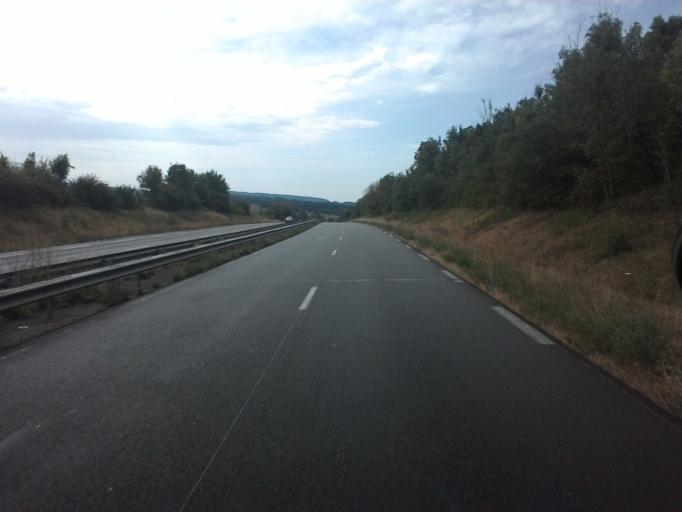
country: FR
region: Franche-Comte
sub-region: Departement du Jura
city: Montmorot
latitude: 46.7384
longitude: 5.5560
